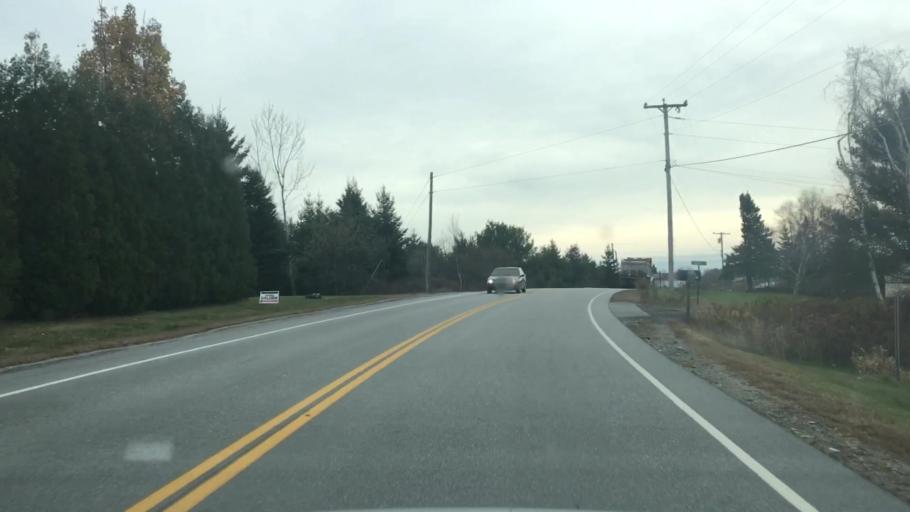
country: US
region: Maine
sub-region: Hancock County
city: Penobscot
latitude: 44.5271
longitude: -68.6667
